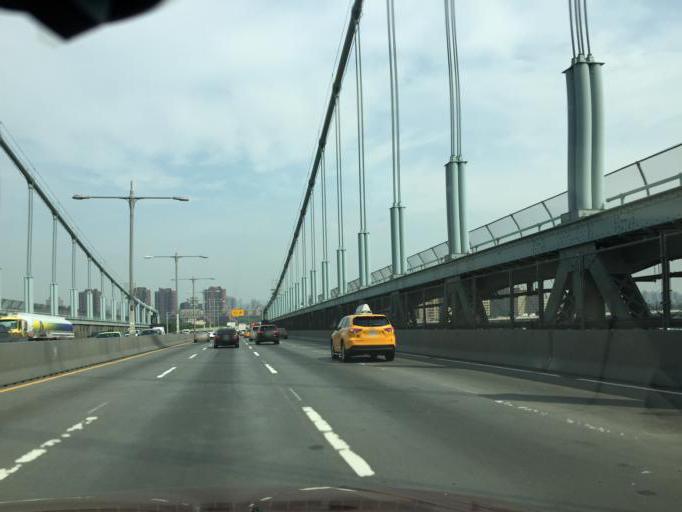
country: US
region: New York
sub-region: New York County
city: Manhattan
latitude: 40.7817
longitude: -73.9281
